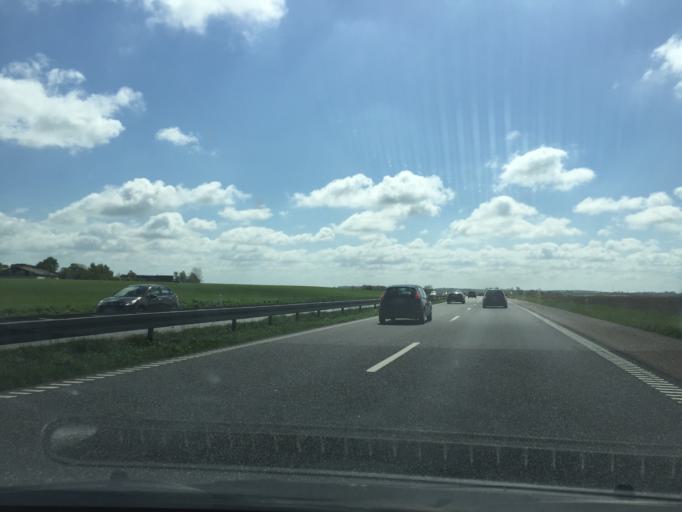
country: DK
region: Zealand
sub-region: Guldborgsund Kommune
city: Norre Alslev
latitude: 54.9249
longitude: 11.9422
